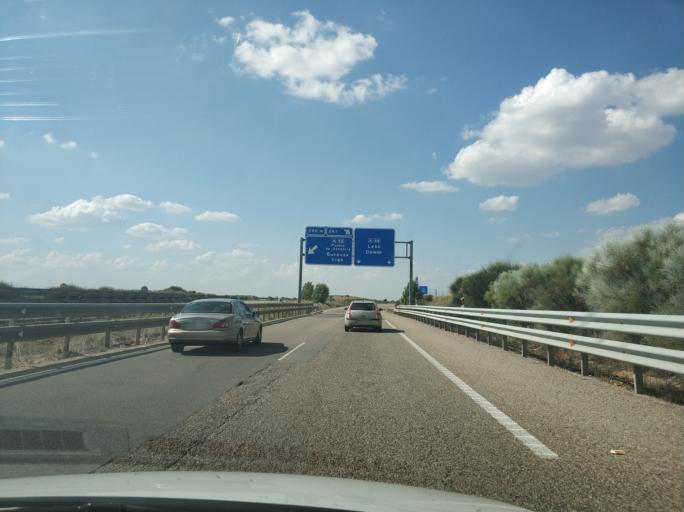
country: ES
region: Castille and Leon
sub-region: Provincia de Zamora
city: San Cristobal de Entrevinas
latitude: 42.0504
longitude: -5.6754
